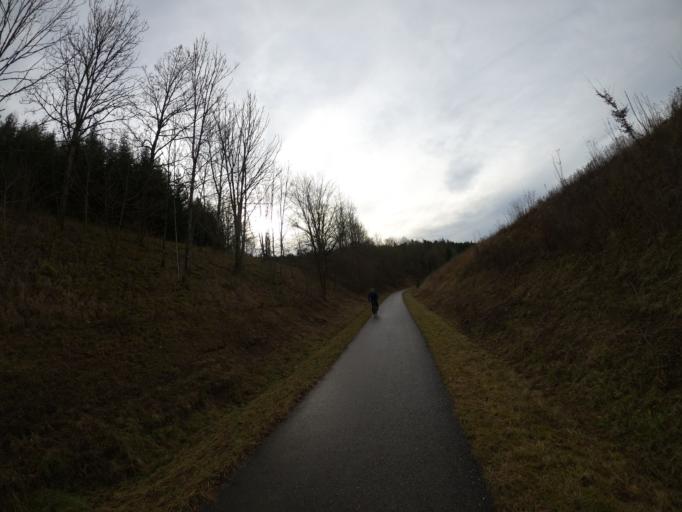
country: DE
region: Baden-Wuerttemberg
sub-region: Regierungsbezirk Stuttgart
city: Ottenbach
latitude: 48.7569
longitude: 9.7514
